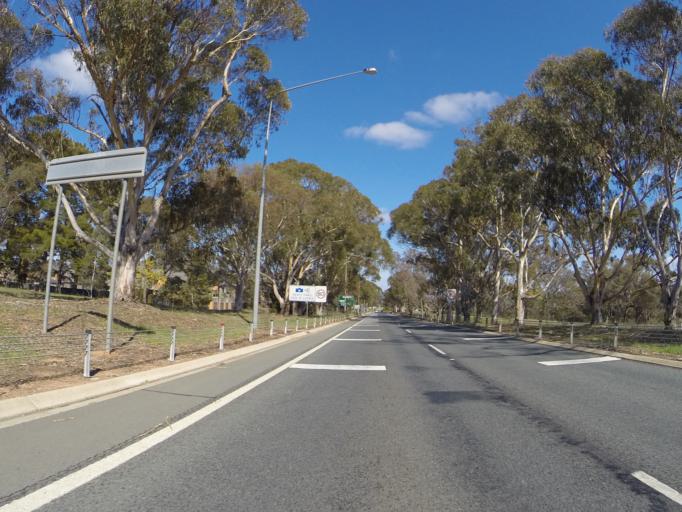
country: AU
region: Australian Capital Territory
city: Kaleen
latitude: -35.2235
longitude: 149.1696
